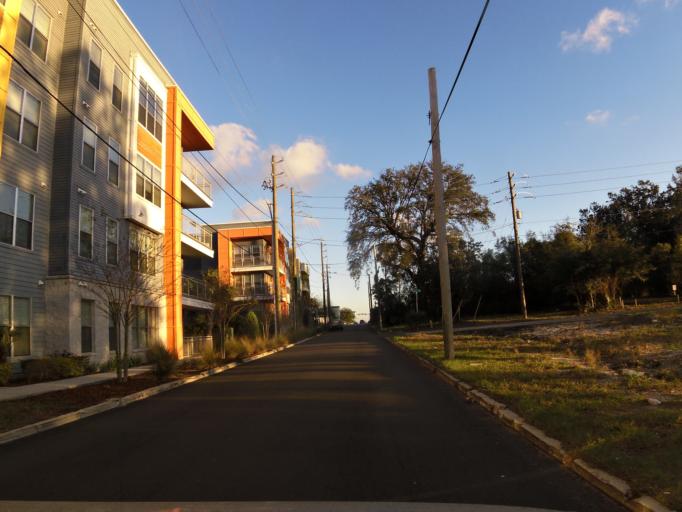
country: US
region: Florida
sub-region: Duval County
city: Jacksonville
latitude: 30.3245
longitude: -81.6736
